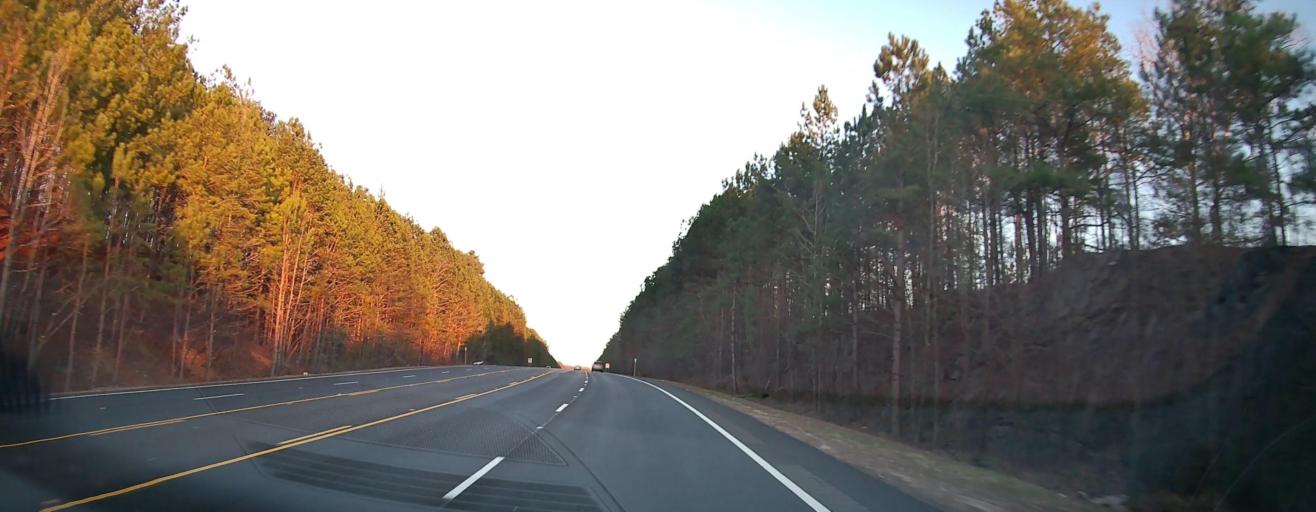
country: US
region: Georgia
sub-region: Fulton County
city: Union City
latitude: 33.5513
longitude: -84.4855
